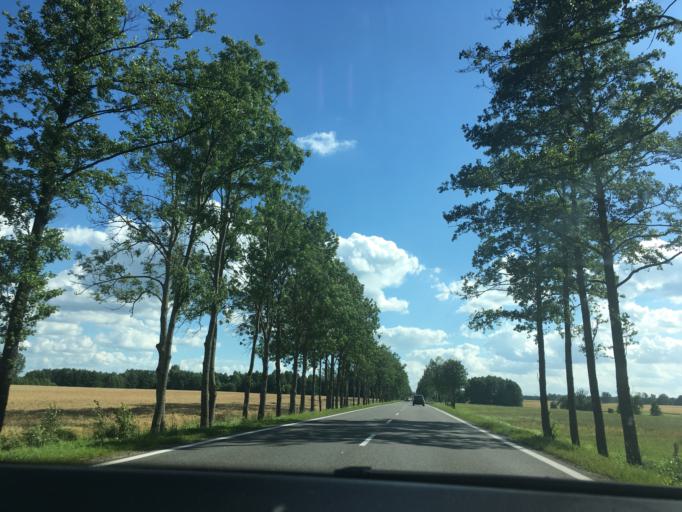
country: PL
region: Podlasie
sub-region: Powiat sokolski
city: Janow
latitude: 53.3837
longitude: 23.1117
